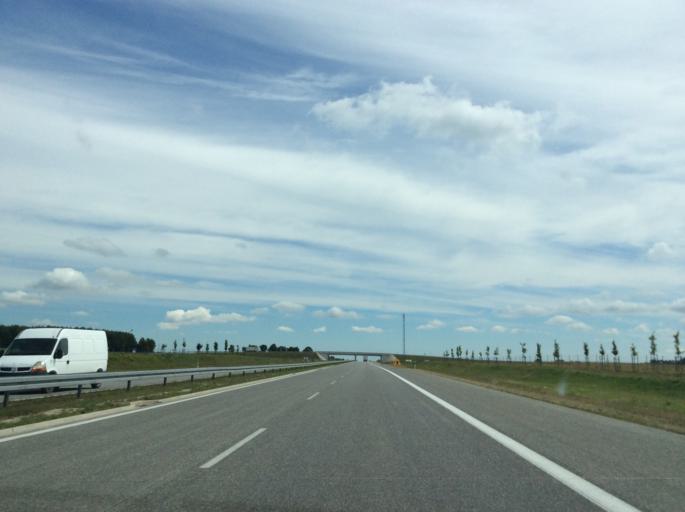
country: PL
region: Lubusz
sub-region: Powiat swiebodzinski
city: Lagow
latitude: 52.2964
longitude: 15.2993
